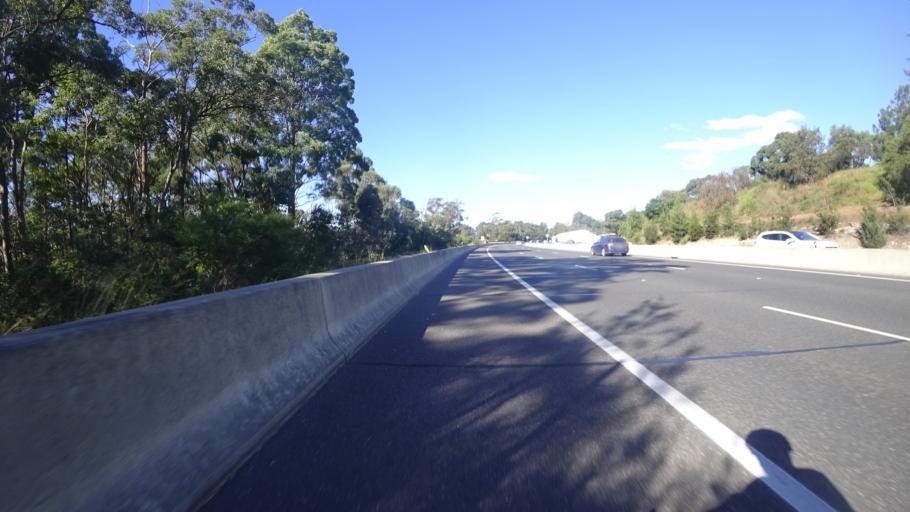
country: AU
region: New South Wales
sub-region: Ryde
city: Macquarie Park
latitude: -33.7645
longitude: 151.1082
